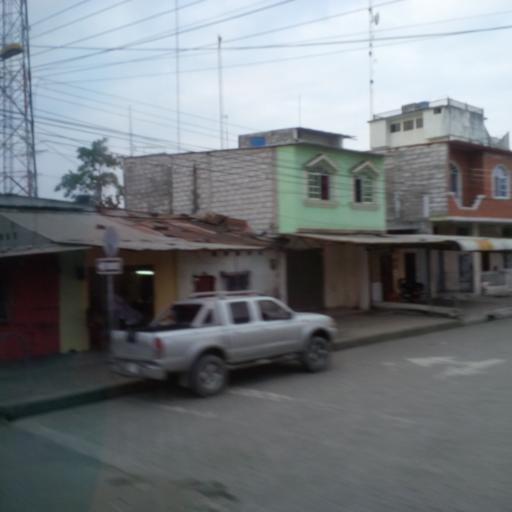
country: EC
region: Canar
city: La Troncal
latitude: -2.3311
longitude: -79.4047
